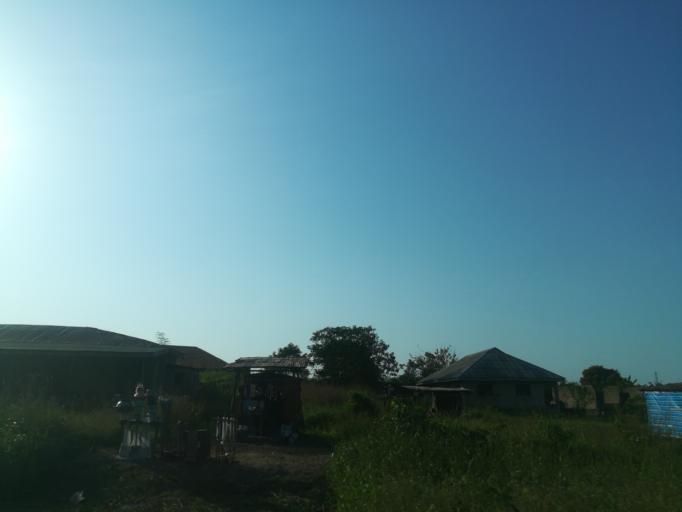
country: NG
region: Ogun
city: Abeokuta
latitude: 7.1888
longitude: 3.2833
